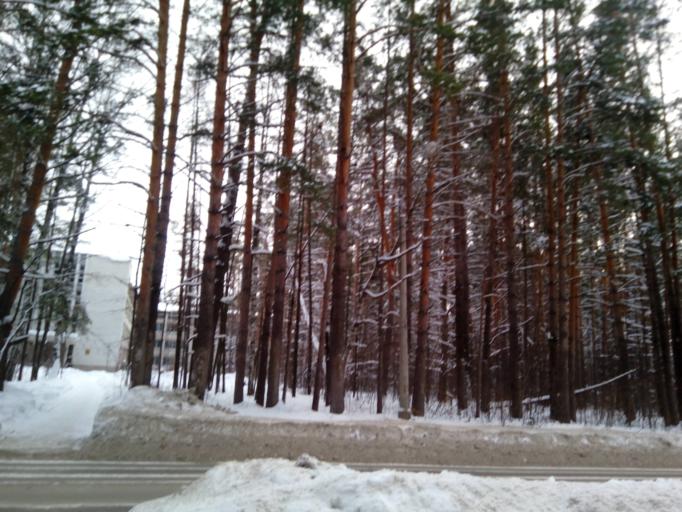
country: RU
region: Novosibirsk
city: Akademgorodok
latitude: 54.8563
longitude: 83.0946
